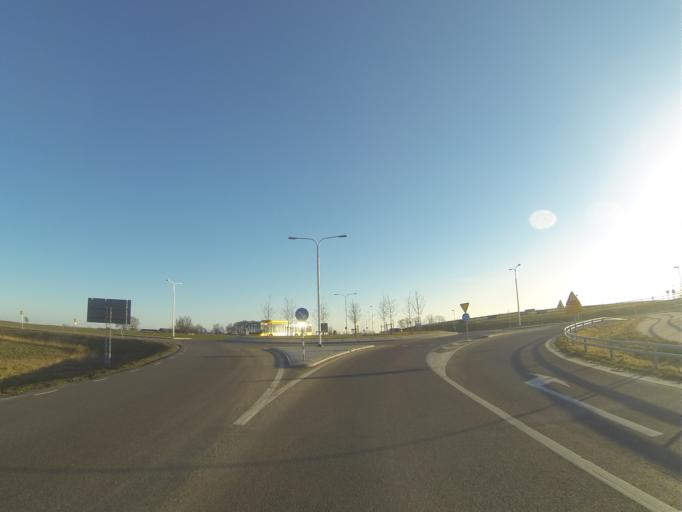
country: SE
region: Skane
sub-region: Malmo
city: Bunkeflostrand
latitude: 55.5455
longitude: 12.9813
